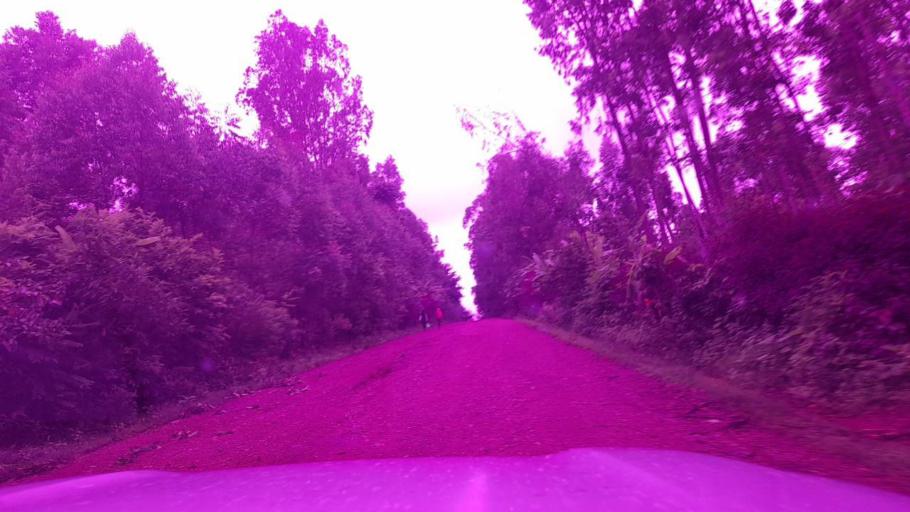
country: ET
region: Southern Nations, Nationalities, and People's Region
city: Bonga
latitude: 7.5824
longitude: 36.0202
